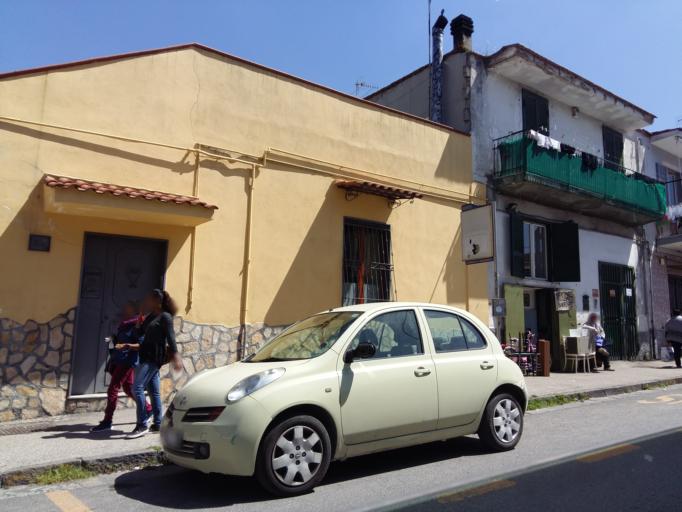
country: IT
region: Campania
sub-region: Provincia di Napoli
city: Mugnano di Napoli
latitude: 40.8872
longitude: 14.2274
